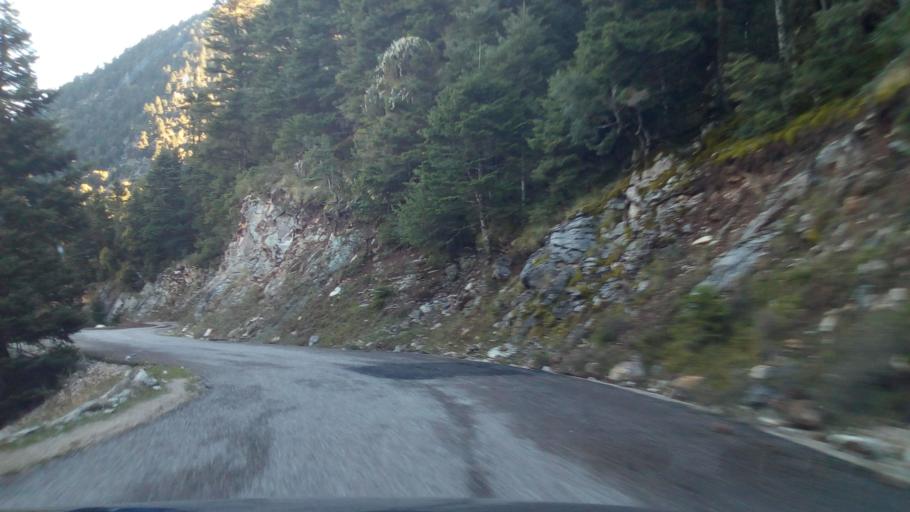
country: GR
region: West Greece
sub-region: Nomos Aitolias kai Akarnanias
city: Nafpaktos
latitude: 38.5397
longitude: 21.8503
